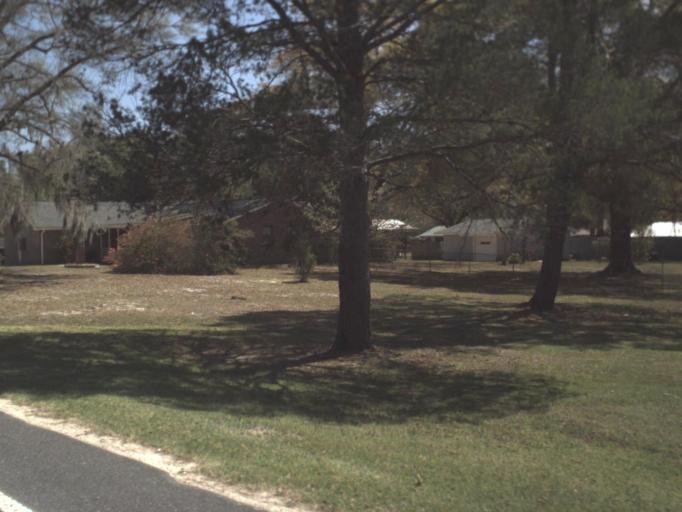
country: US
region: Florida
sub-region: Walton County
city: DeFuniak Springs
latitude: 30.7318
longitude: -85.9444
